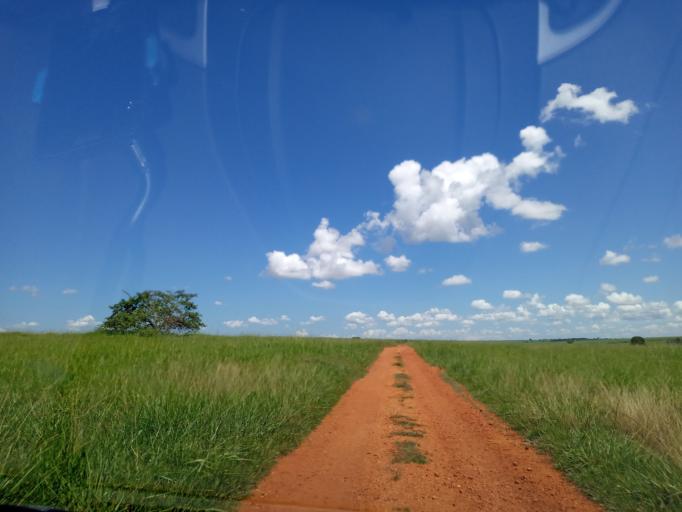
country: BR
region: Goias
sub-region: Itumbiara
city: Itumbiara
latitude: -18.3990
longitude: -49.1284
